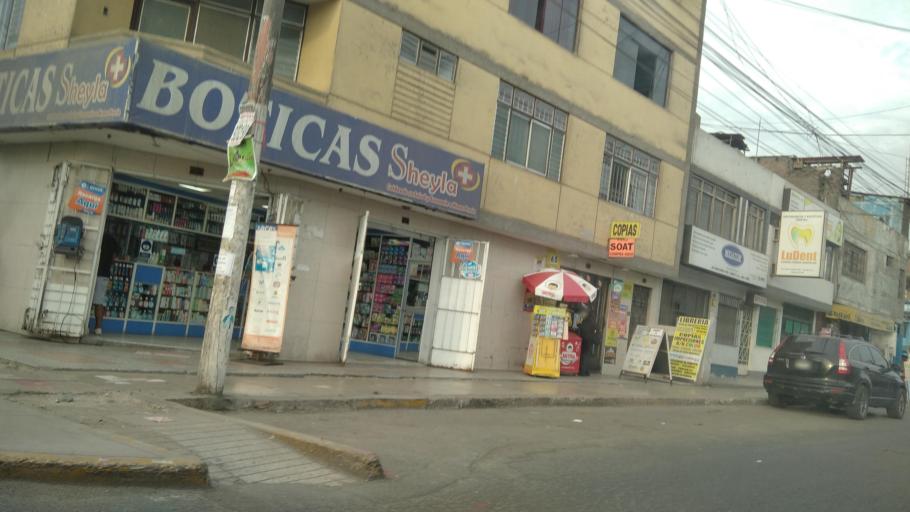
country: PE
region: Lima
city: Lima
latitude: -12.0246
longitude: -76.9968
